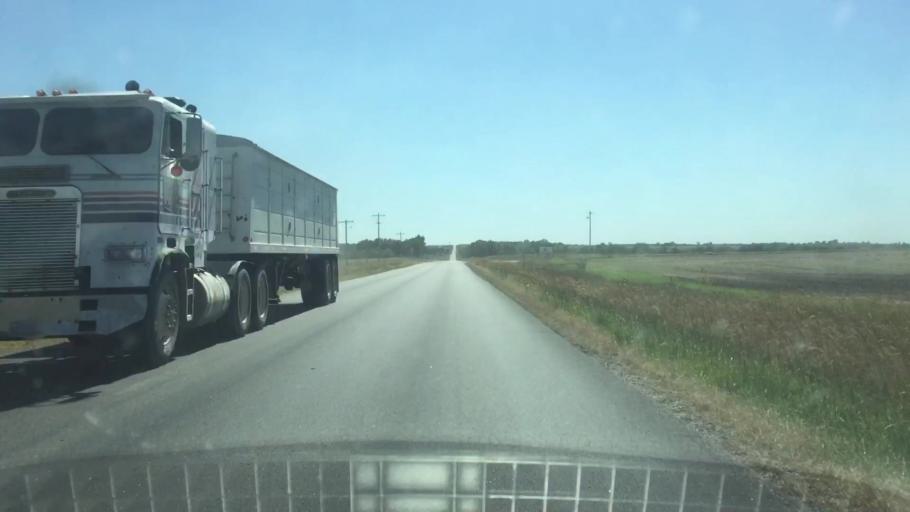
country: US
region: Kansas
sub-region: Marshall County
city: Marysville
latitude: 39.9450
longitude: -96.6009
